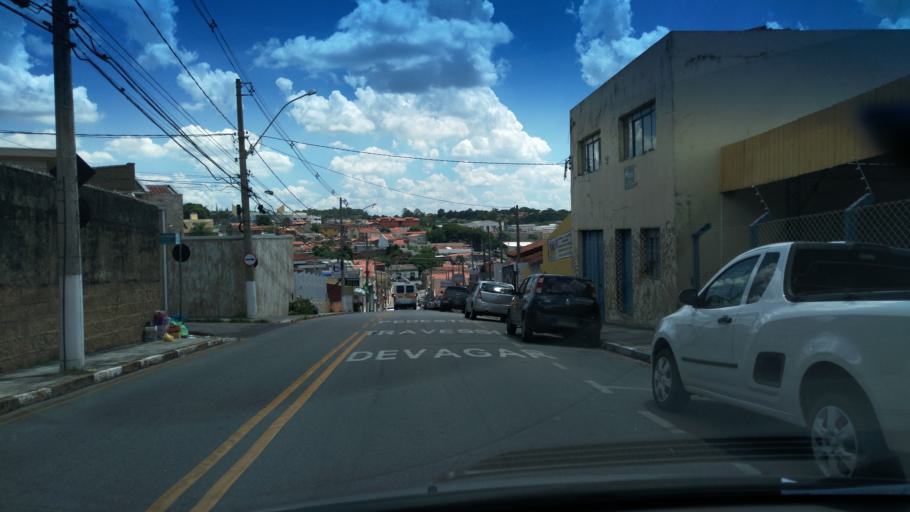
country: BR
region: Sao Paulo
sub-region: Vinhedo
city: Vinhedo
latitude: -23.0279
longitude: -46.9763
